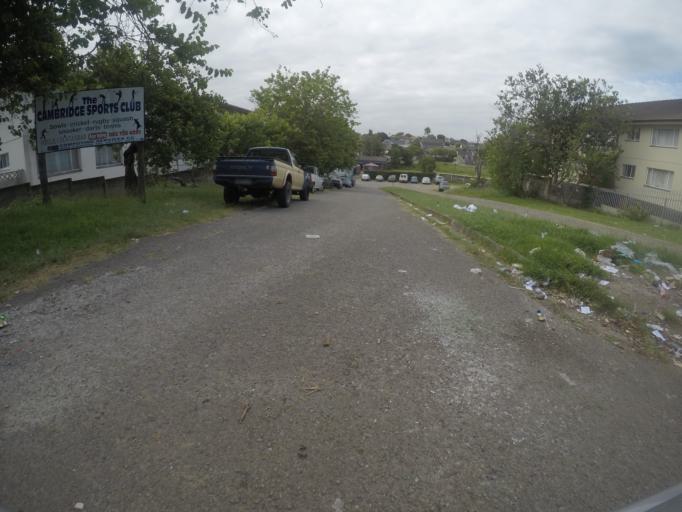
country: ZA
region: Eastern Cape
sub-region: Buffalo City Metropolitan Municipality
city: East London
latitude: -32.9836
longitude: 27.8937
